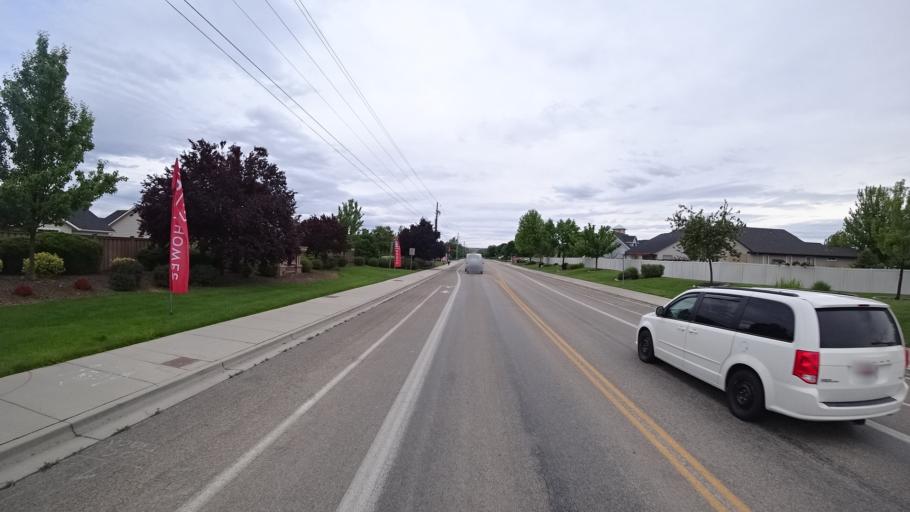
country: US
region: Idaho
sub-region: Ada County
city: Star
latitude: 43.7000
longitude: -116.4933
